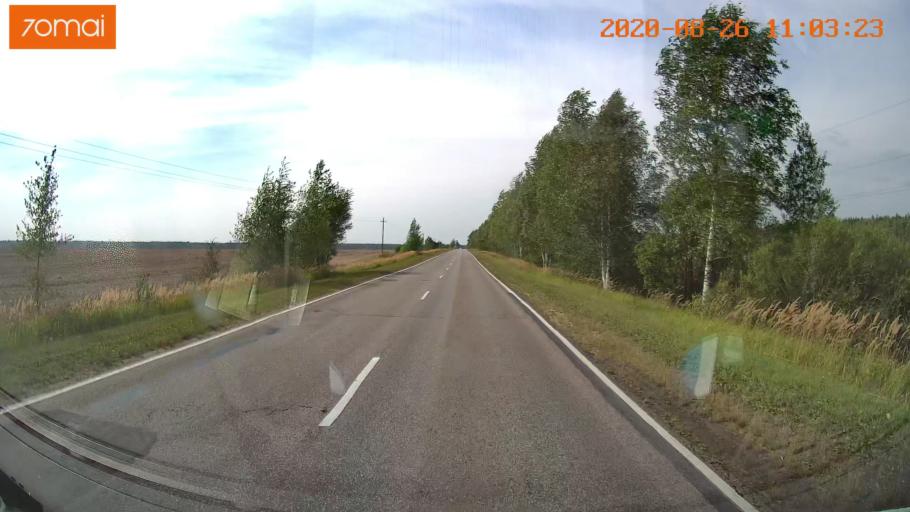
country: RU
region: Rjazan
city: Izhevskoye
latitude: 54.5411
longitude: 41.2120
